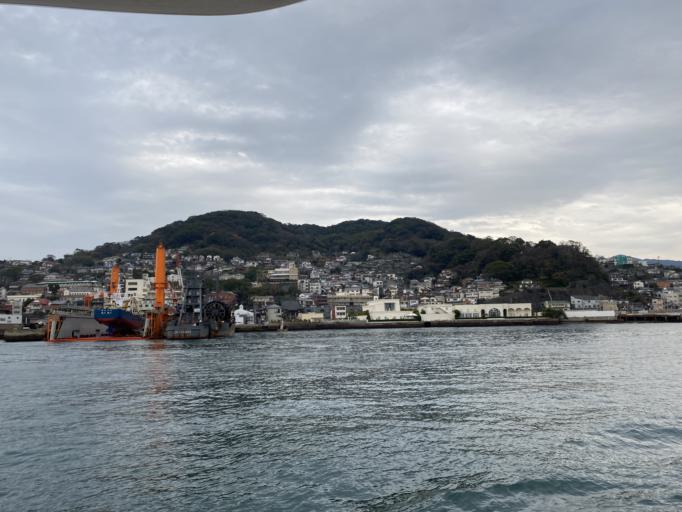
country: JP
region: Nagasaki
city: Nagasaki-shi
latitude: 32.7333
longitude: 129.8621
